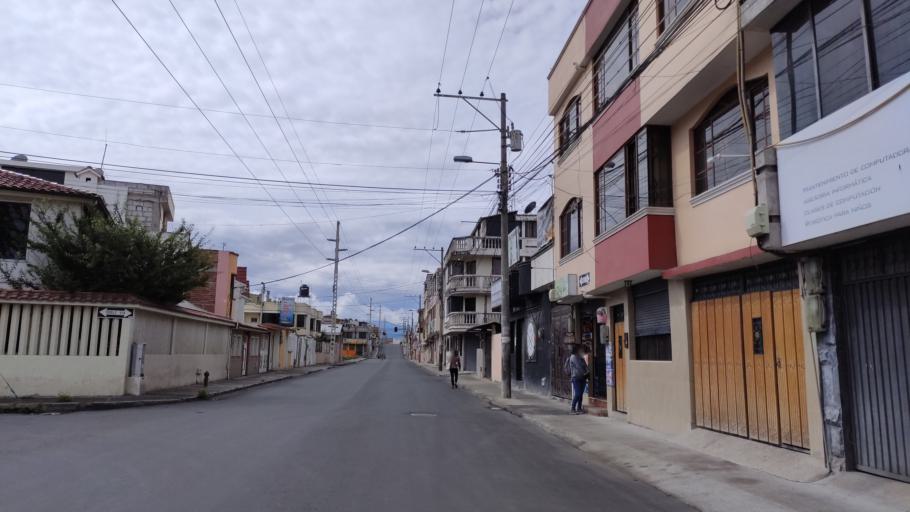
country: EC
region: Chimborazo
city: Riobamba
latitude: -1.6567
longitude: -78.6443
